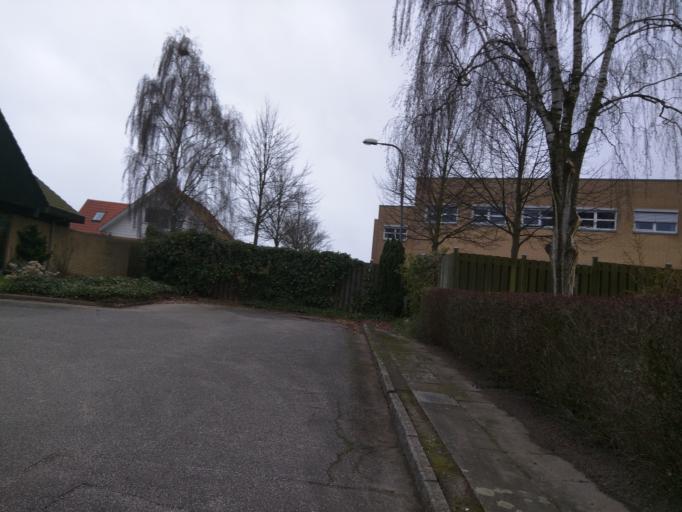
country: DK
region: South Denmark
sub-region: Fredericia Kommune
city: Snoghoj
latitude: 55.5424
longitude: 9.7165
